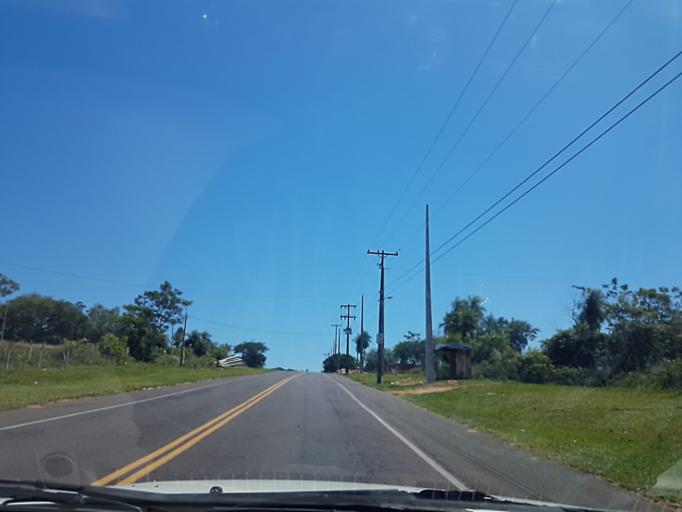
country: PY
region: Cordillera
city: Altos
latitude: -25.2540
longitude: -57.2422
